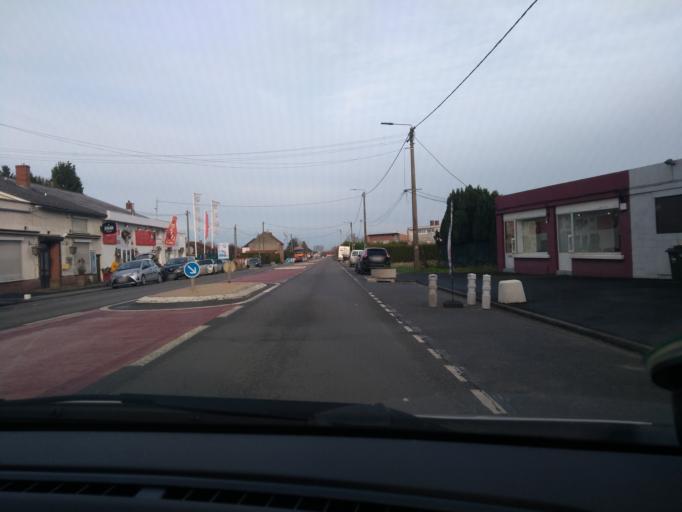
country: BE
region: Wallonia
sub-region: Province du Hainaut
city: Quevy-le-Petit
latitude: 50.3359
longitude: 3.9727
